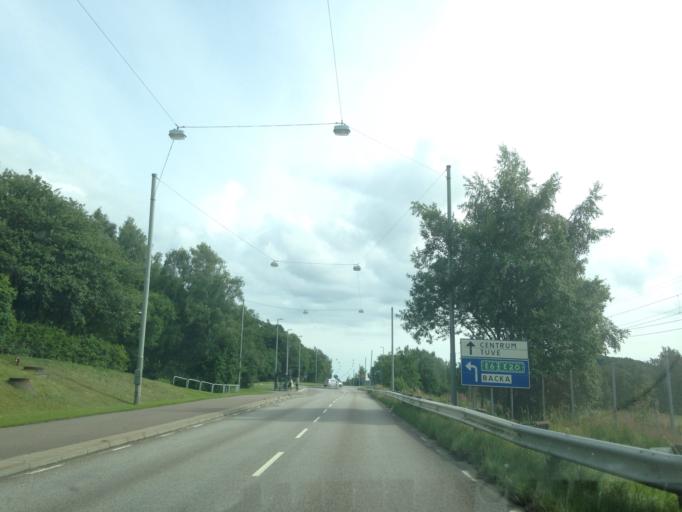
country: SE
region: Vaestra Goetaland
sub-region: Goteborg
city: Goeteborg
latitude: 57.7548
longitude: 11.9472
